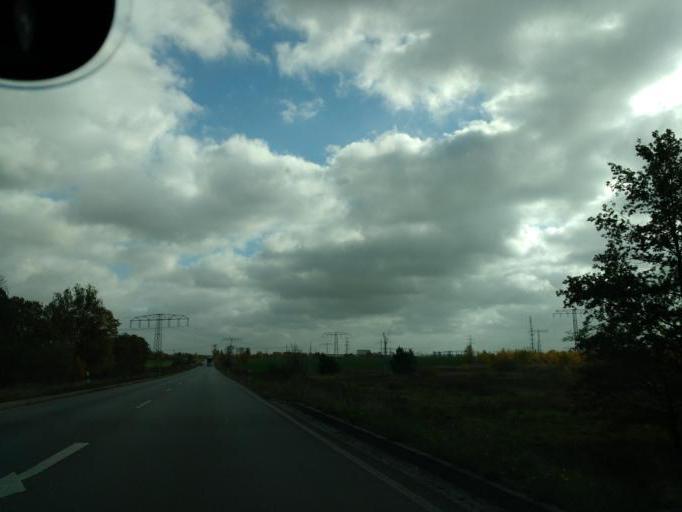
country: DE
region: Brandenburg
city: Neuenhagen
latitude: 52.5502
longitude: 13.6988
